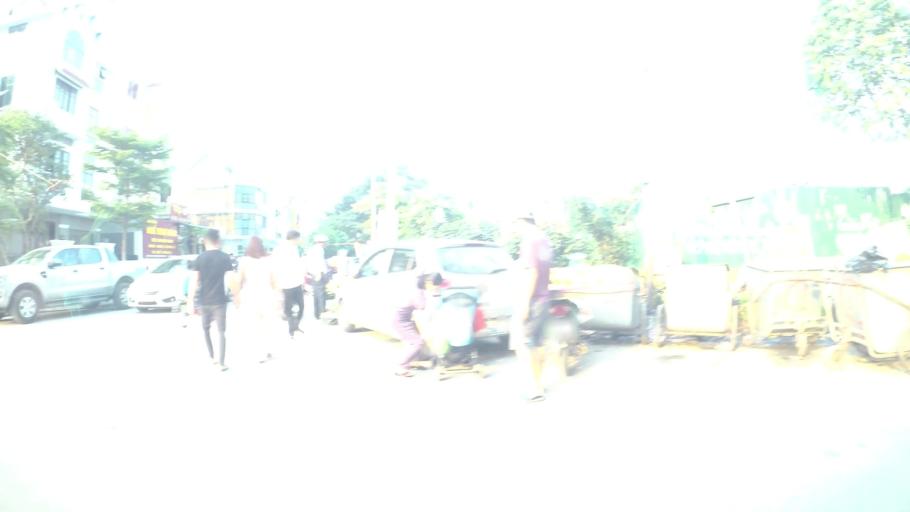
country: VN
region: Ha Noi
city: Thanh Xuan
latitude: 20.9739
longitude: 105.8202
